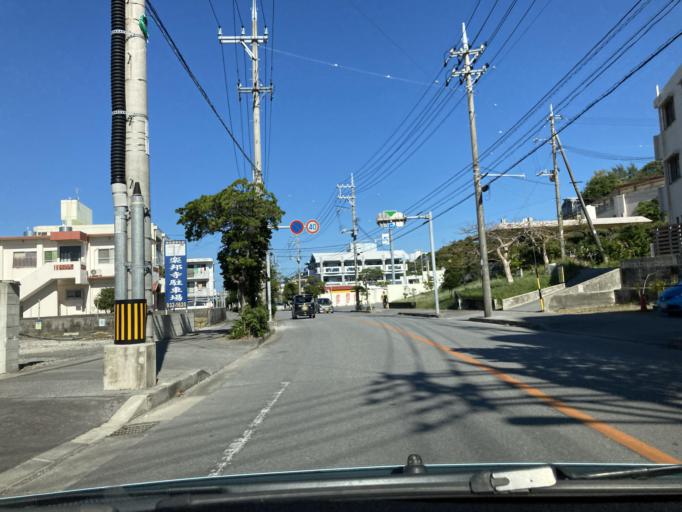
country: JP
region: Okinawa
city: Okinawa
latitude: 26.3192
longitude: 127.8018
